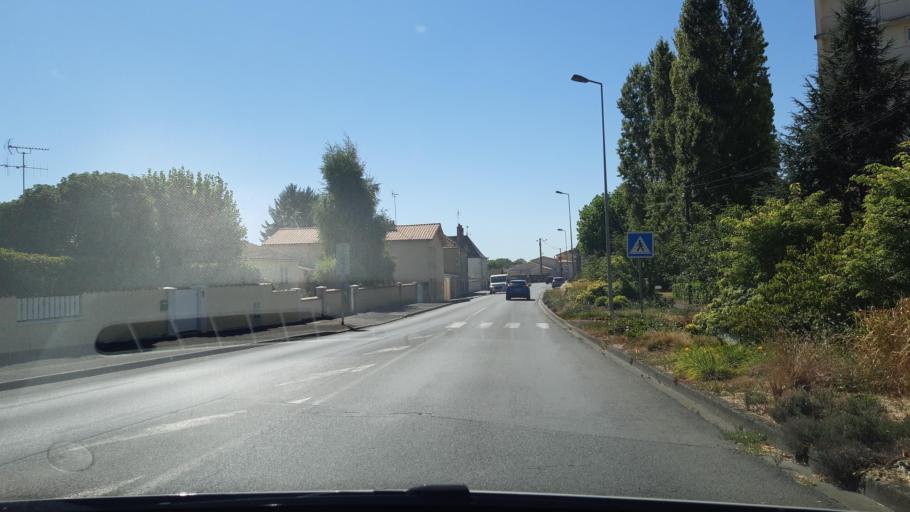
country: FR
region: Poitou-Charentes
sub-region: Departement des Deux-Sevres
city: Exireuil
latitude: 46.4185
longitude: -0.2040
